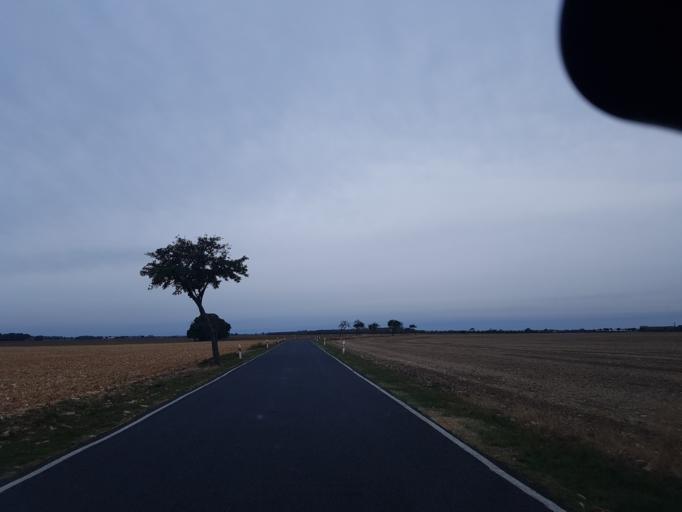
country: DE
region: Saxony
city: Belgern
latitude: 51.4990
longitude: 13.1733
